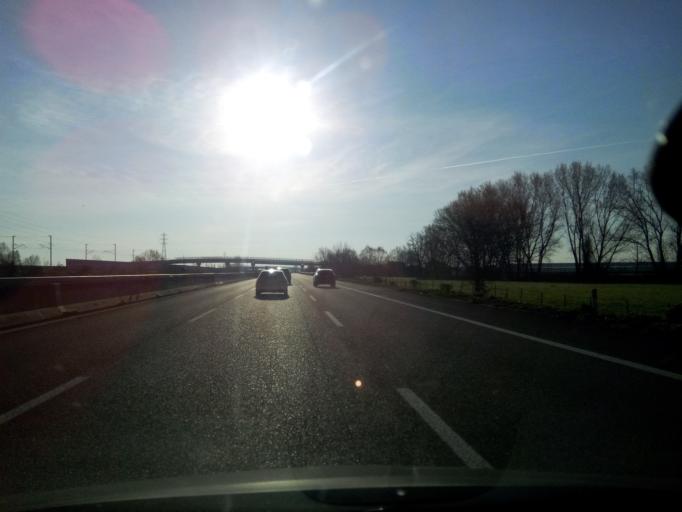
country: IT
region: Emilia-Romagna
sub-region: Provincia di Parma
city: Soragna
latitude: 44.8862
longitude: 10.1097
